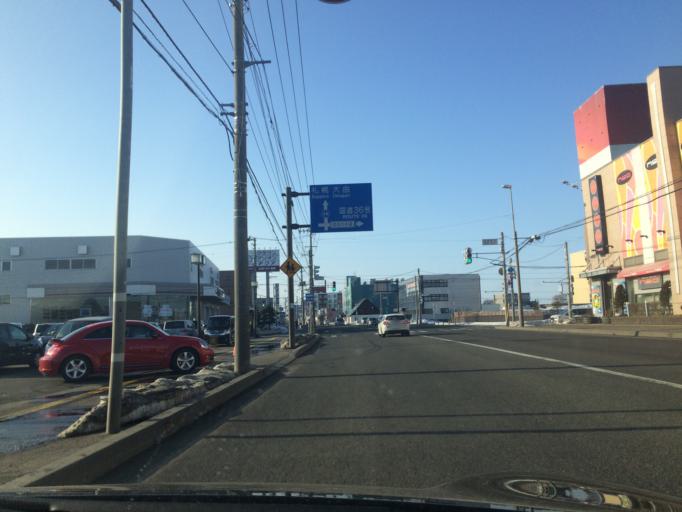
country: JP
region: Hokkaido
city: Chitose
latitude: 42.8761
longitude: 141.5829
